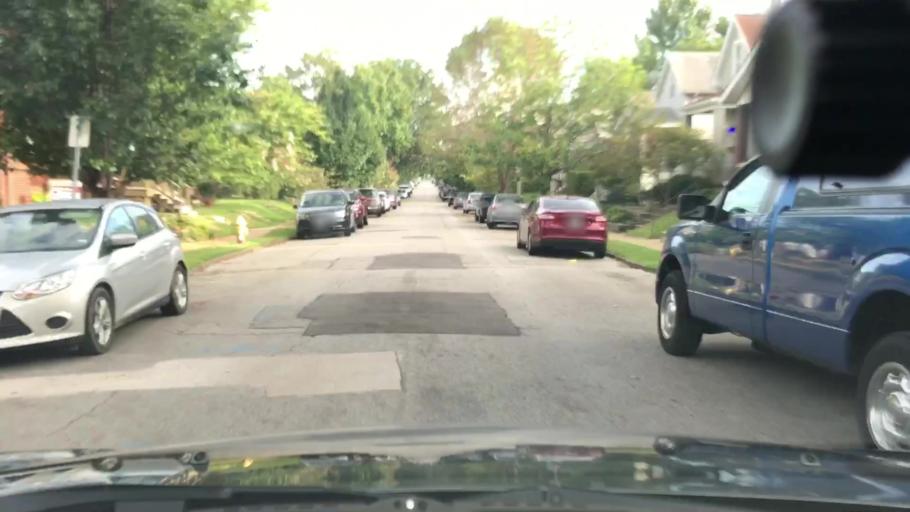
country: US
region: Missouri
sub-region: Saint Louis County
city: Lemay
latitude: 38.5785
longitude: -90.2806
